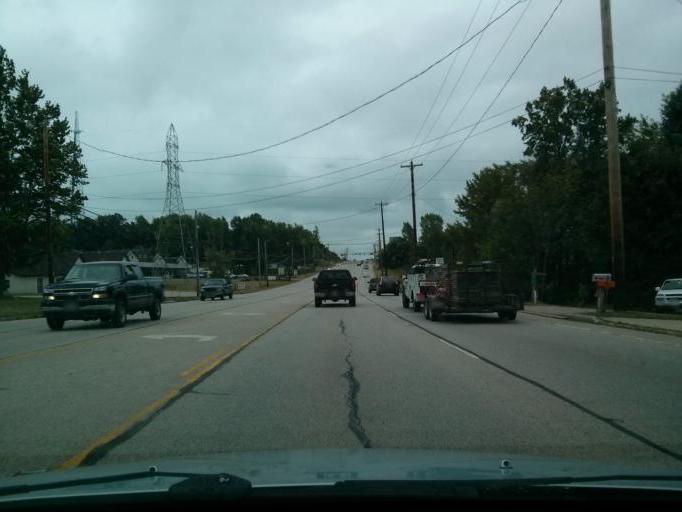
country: US
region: Ohio
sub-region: Portage County
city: Brimfield
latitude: 41.1139
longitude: -81.3479
